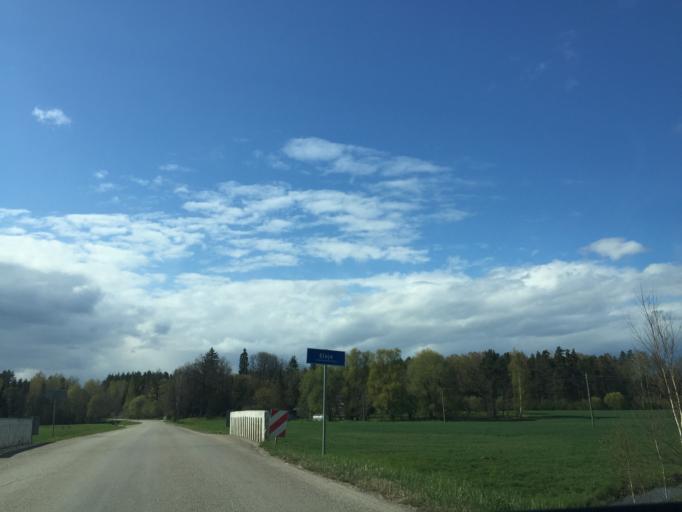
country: LV
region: Jelgava
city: Jelgava
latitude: 56.5656
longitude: 23.7572
